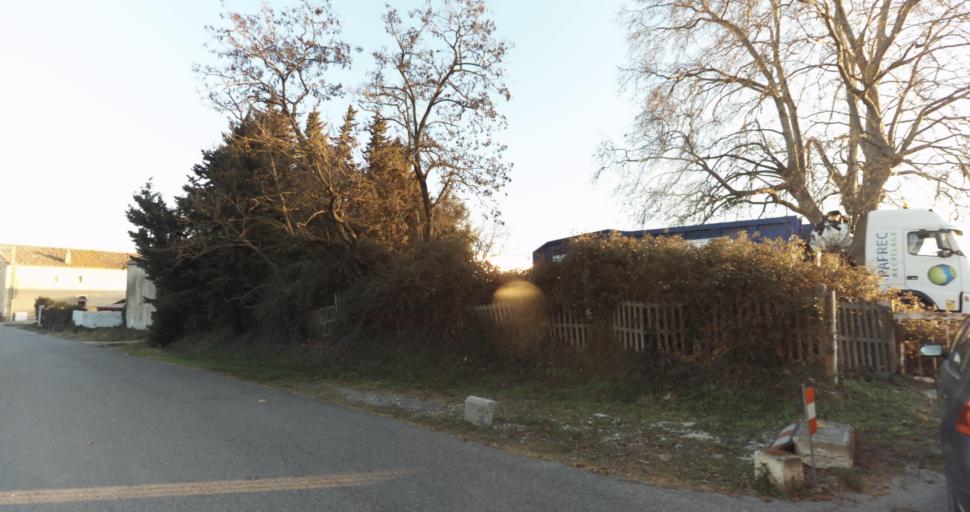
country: FR
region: Provence-Alpes-Cote d'Azur
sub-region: Departement des Bouches-du-Rhone
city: Rognonas
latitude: 43.8964
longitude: 4.7832
